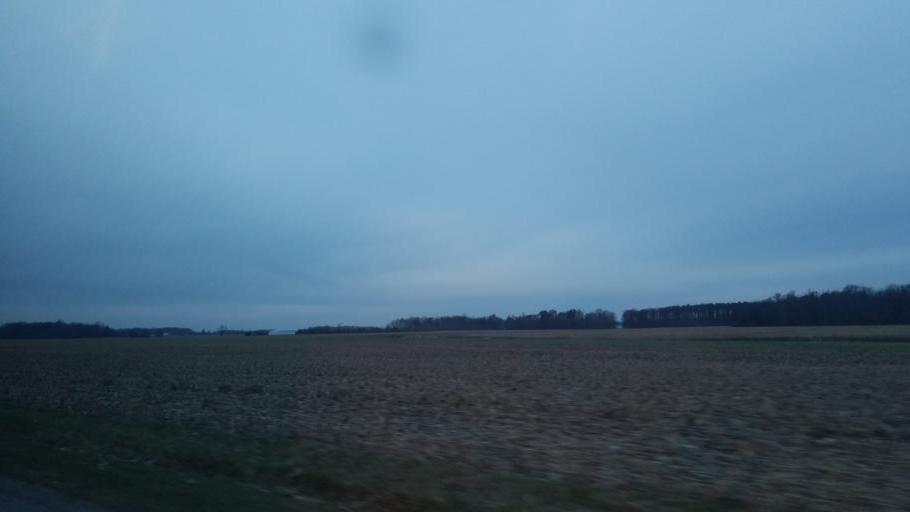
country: US
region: Indiana
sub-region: Adams County
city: Decatur
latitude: 40.7585
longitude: -85.0057
